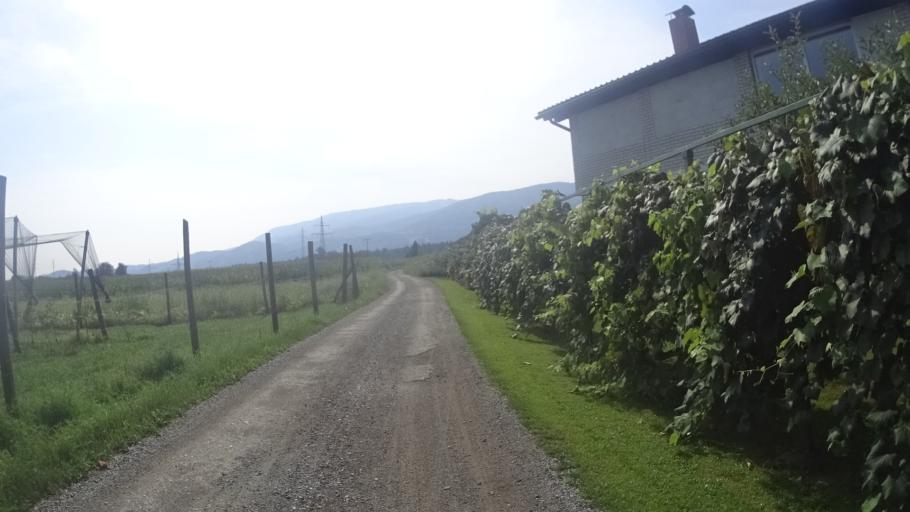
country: SI
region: Selnica ob Dravi
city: Selnica ob Dravi
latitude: 46.5463
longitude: 15.4722
